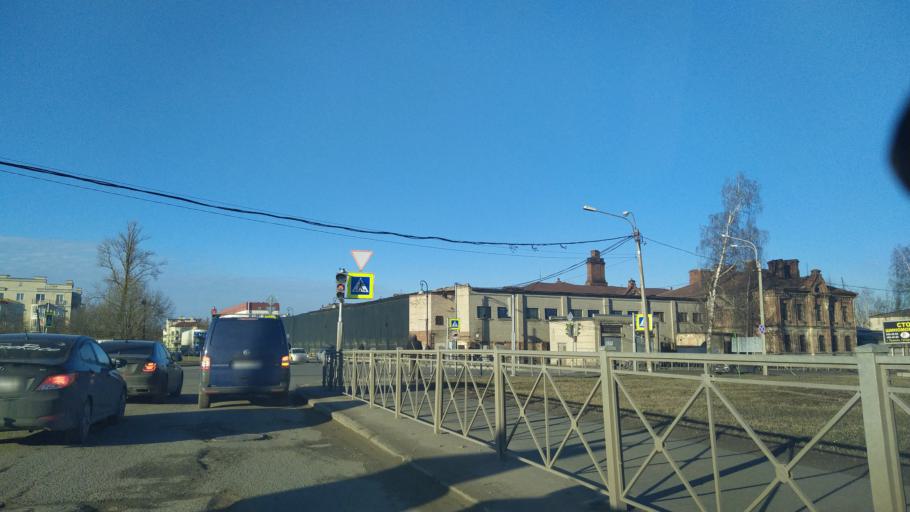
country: RU
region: St.-Petersburg
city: Pushkin
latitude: 59.7004
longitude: 30.3944
